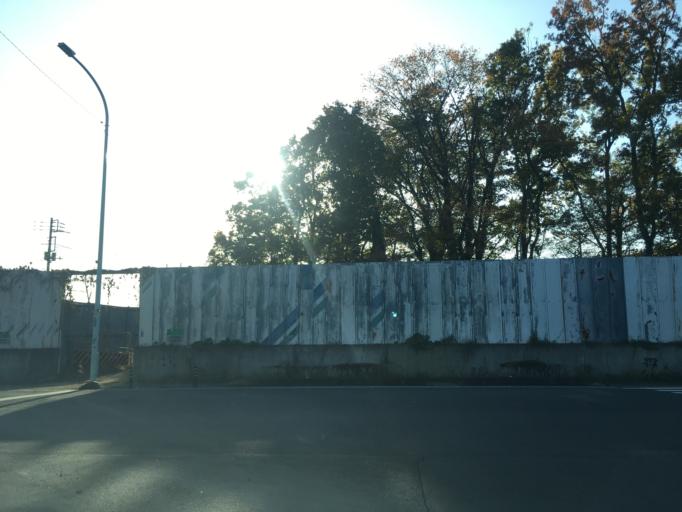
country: JP
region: Saitama
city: Tokorozawa
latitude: 35.8027
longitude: 139.4899
